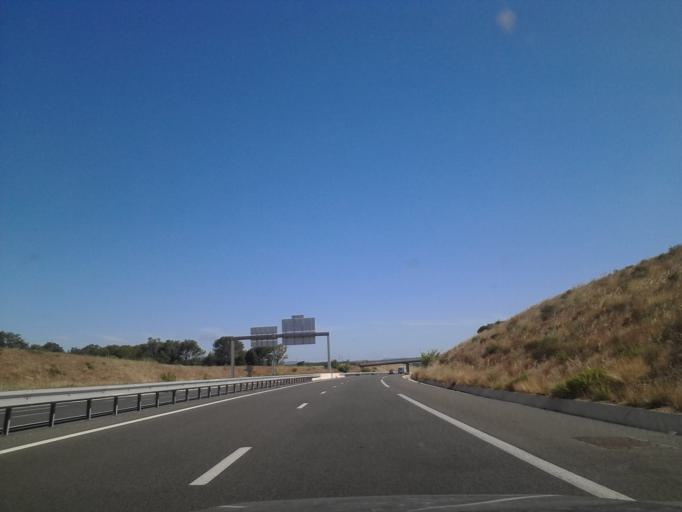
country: FR
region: Languedoc-Roussillon
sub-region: Departement de l'Herault
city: Boujan-sur-Libron
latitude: 43.3600
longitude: 3.2739
